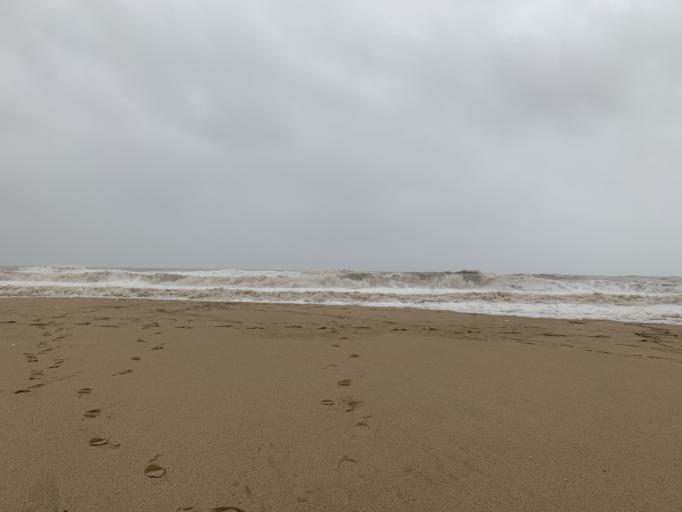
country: ES
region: Catalonia
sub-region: Provincia de Barcelona
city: Mataro
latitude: 41.5351
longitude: 2.4504
